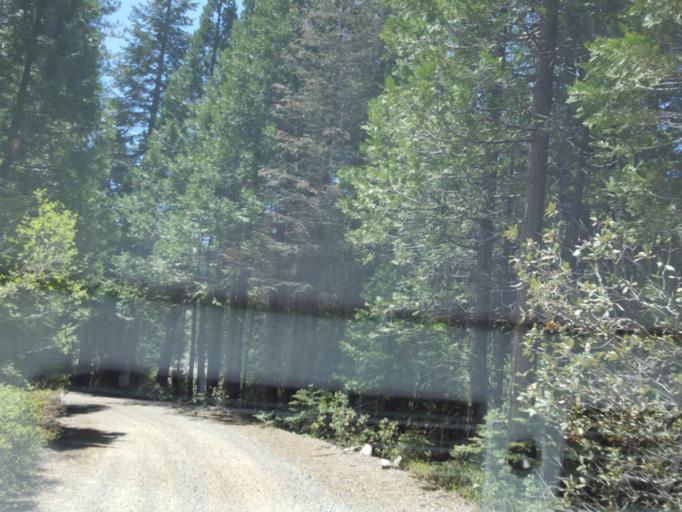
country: US
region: California
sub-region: Madera County
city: Oakhurst
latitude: 37.3480
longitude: -119.4877
